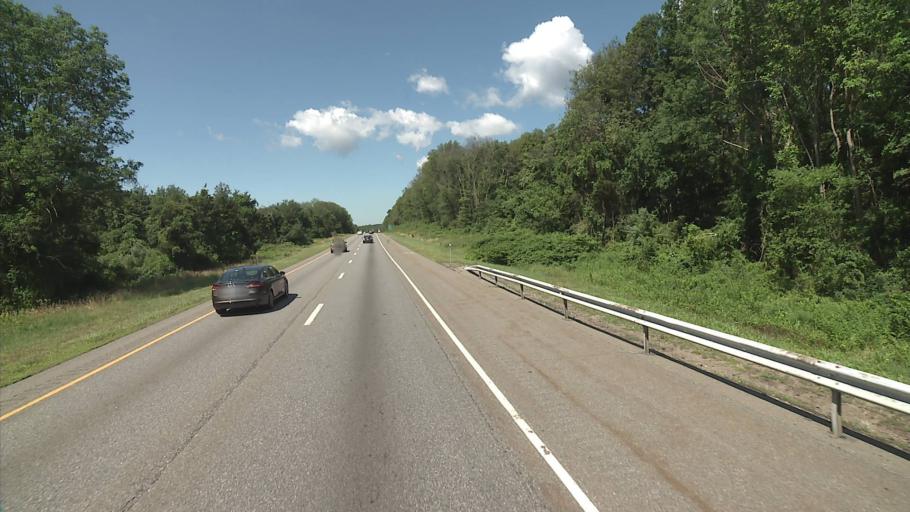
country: US
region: Connecticut
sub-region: New London County
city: Old Mystic
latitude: 41.3747
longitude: -71.9185
